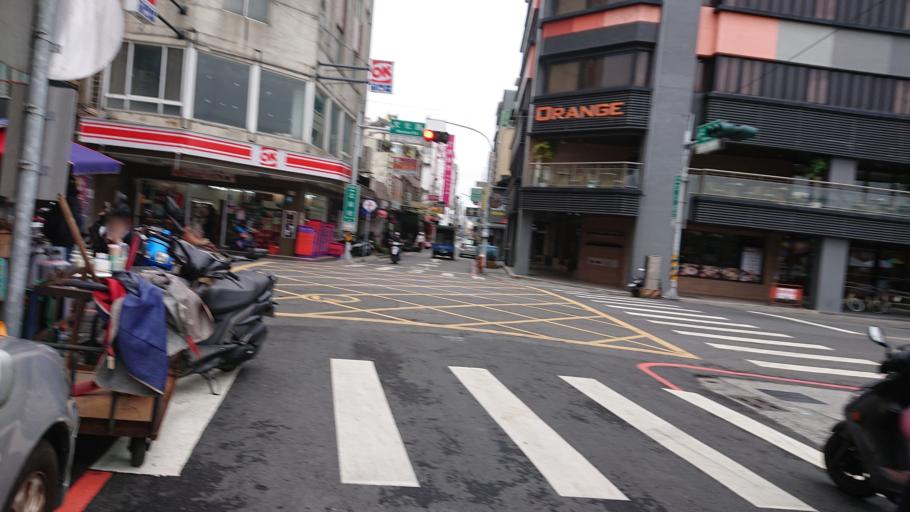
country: TW
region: Taiwan
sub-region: Chiayi
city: Jiayi Shi
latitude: 23.4809
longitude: 120.4495
